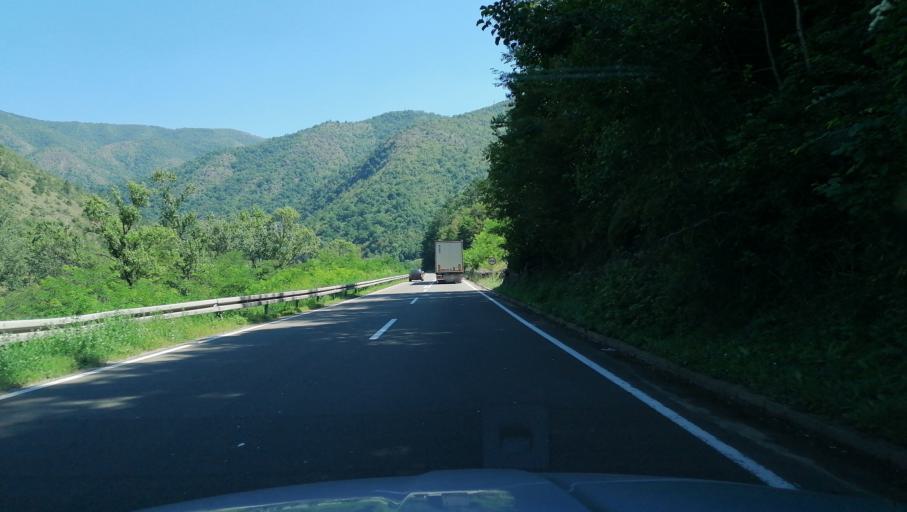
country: RS
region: Central Serbia
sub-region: Raski Okrug
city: Kraljevo
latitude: 43.5499
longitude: 20.6109
